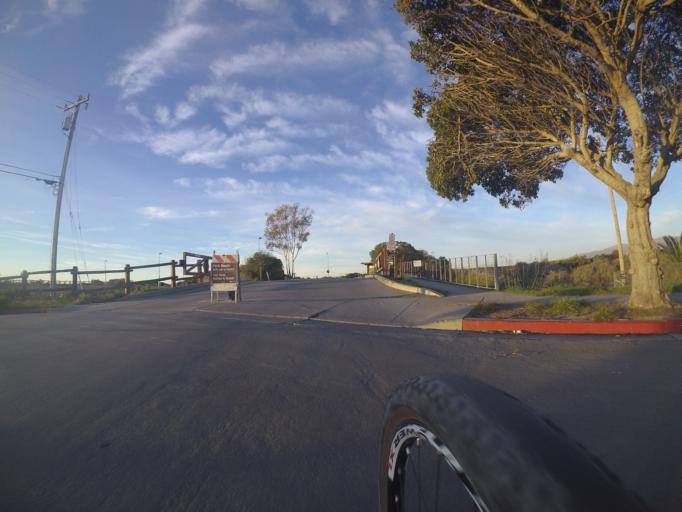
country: US
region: California
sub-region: Santa Clara County
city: Milpitas
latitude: 37.4292
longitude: -121.9792
